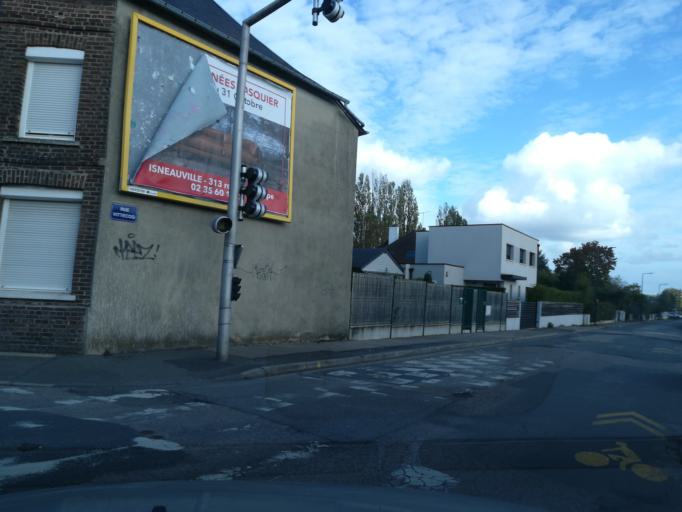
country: FR
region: Haute-Normandie
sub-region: Departement de la Seine-Maritime
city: Bois-Guillaume
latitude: 49.4738
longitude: 1.1243
